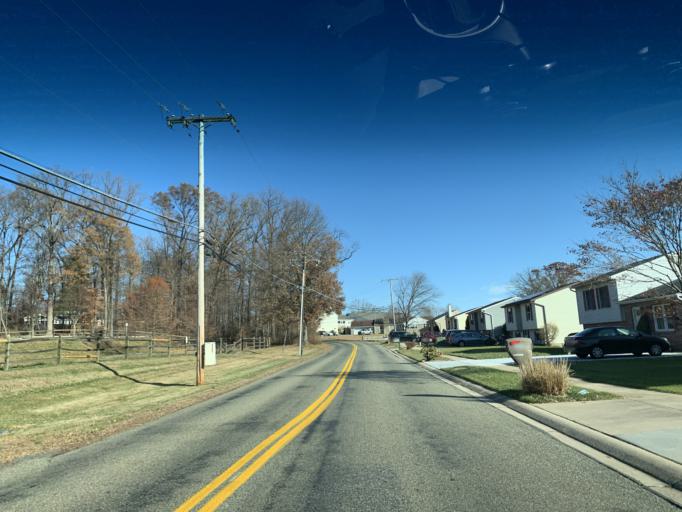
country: US
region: Maryland
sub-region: Harford County
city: Bel Air South
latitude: 39.4895
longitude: -76.3137
